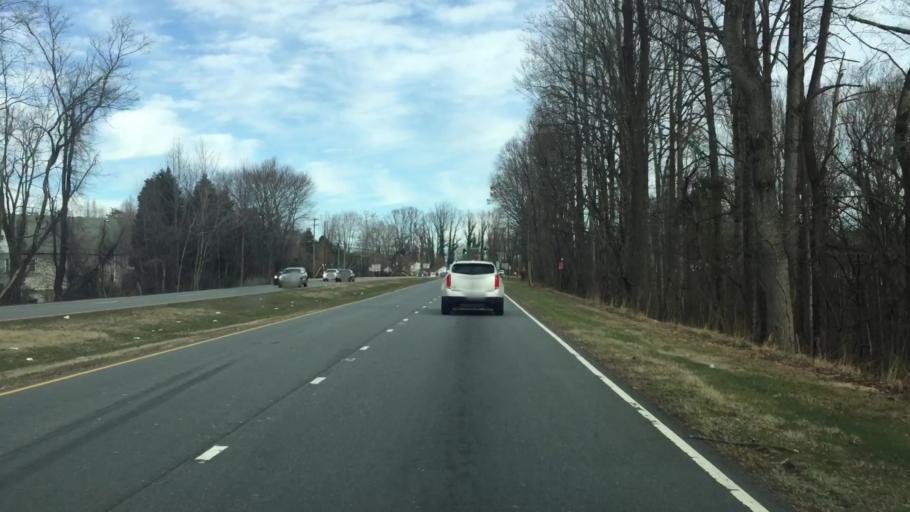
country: US
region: North Carolina
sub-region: Forsyth County
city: Winston-Salem
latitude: 36.1133
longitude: -80.1880
